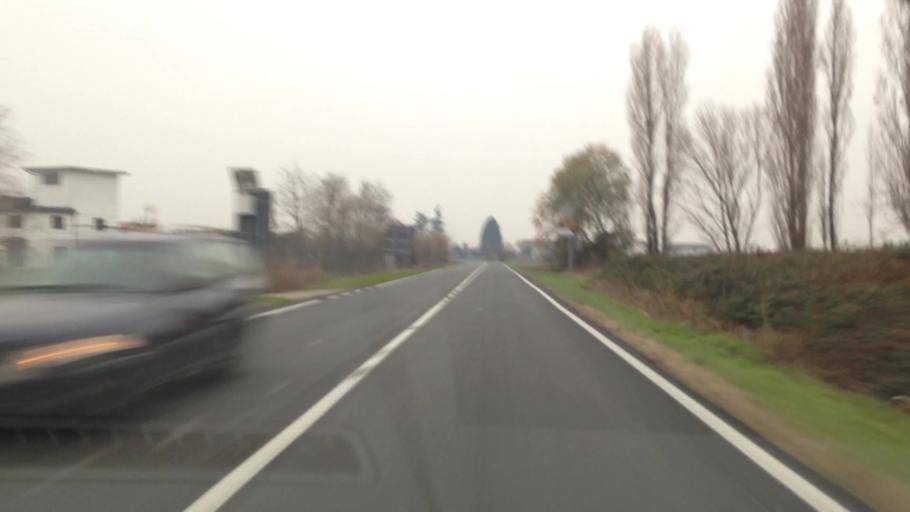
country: IT
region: Piedmont
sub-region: Provincia di Vercelli
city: Livorno Ferraris
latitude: 45.2861
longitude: 8.0622
